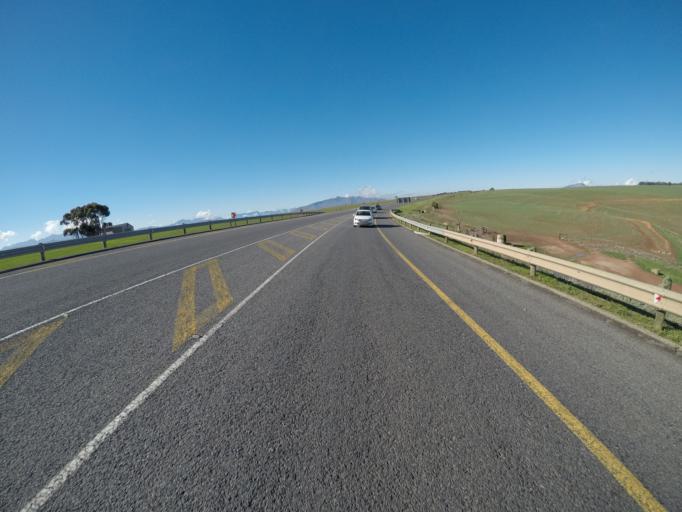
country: ZA
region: Western Cape
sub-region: Overberg District Municipality
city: Caledon
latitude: -34.2224
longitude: 19.2821
